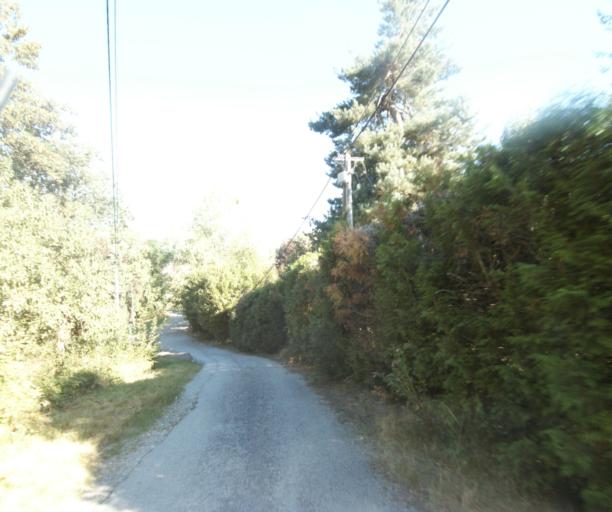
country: FR
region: Lorraine
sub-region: Departement des Vosges
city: Epinal
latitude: 48.1671
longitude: 6.4624
